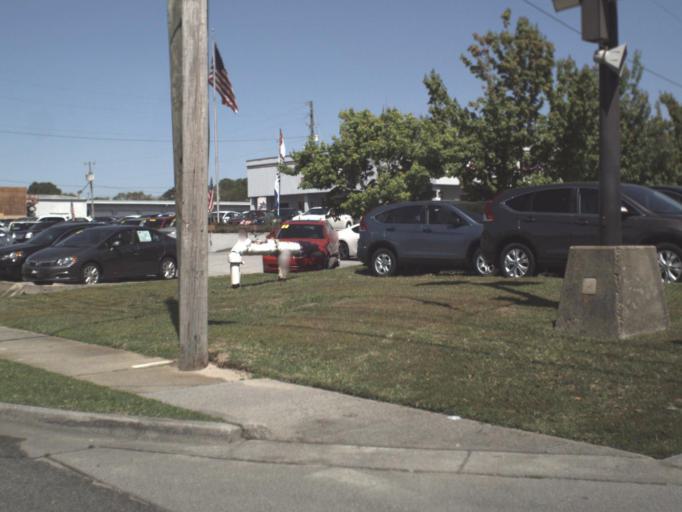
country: US
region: Florida
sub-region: Okaloosa County
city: Fort Walton Beach
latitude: 30.4060
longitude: -86.6283
